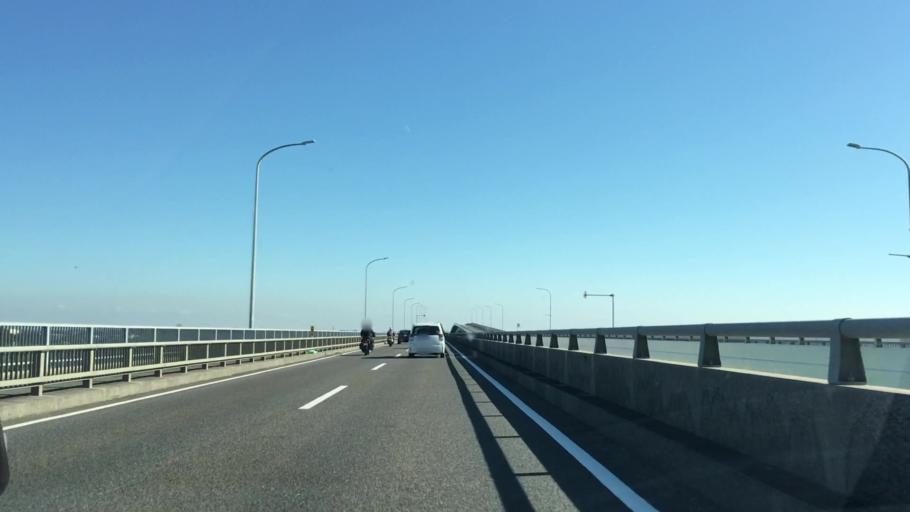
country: JP
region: Aichi
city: Tahara
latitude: 34.6935
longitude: 137.2989
